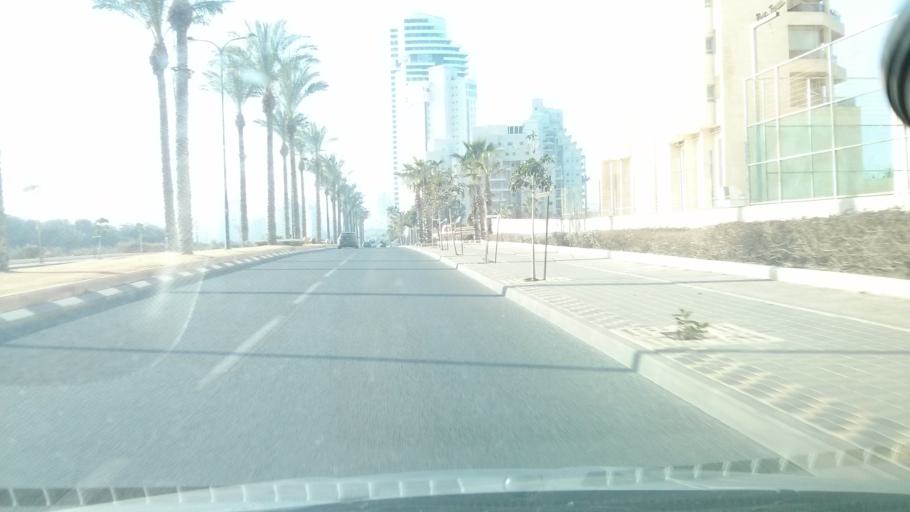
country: IL
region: Central District
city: Netanya
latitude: 32.3092
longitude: 34.8469
